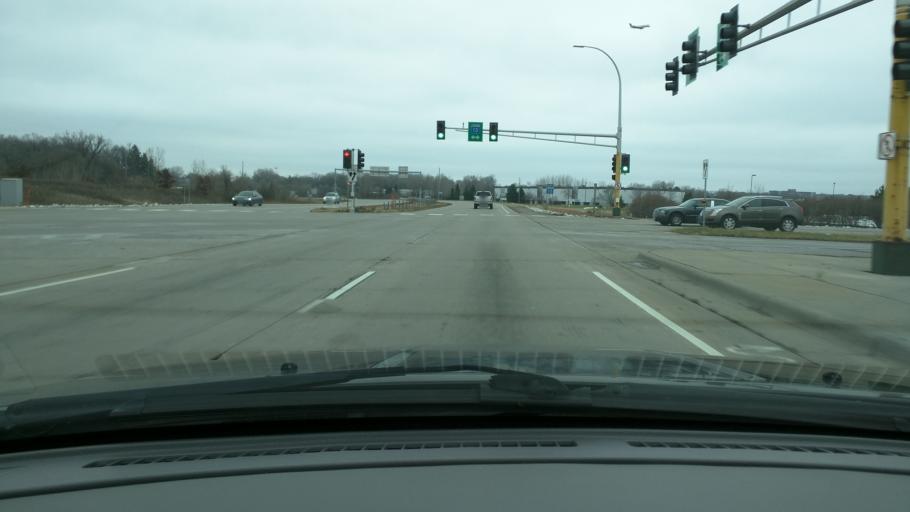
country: US
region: Minnesota
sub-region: Dakota County
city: Mendota Heights
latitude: 44.8741
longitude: -93.1635
